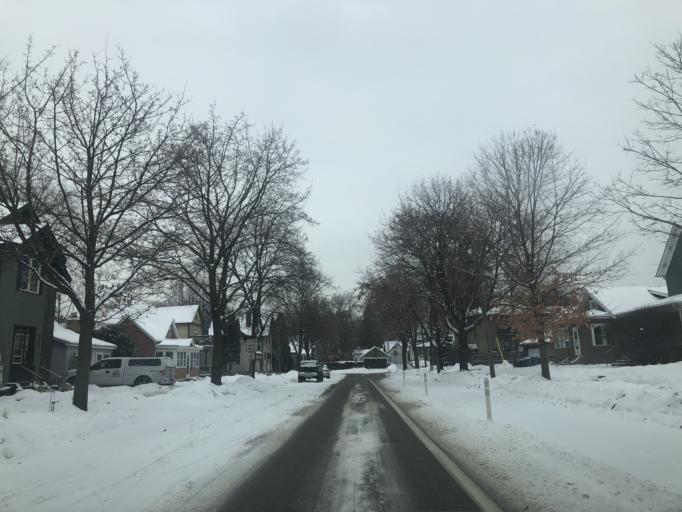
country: US
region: Minnesota
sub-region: Hennepin County
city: Richfield
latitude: 44.9315
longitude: -93.2798
